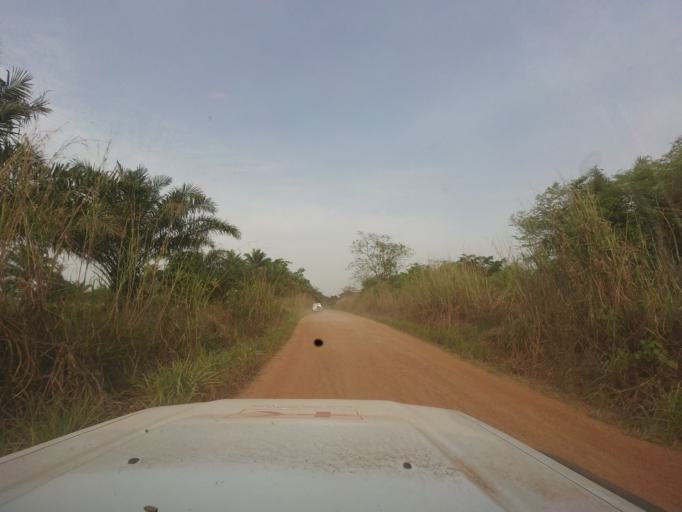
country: GN
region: Nzerekore
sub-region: Prefecture de Guekedou
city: Gueckedou
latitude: 8.5236
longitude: -10.1896
